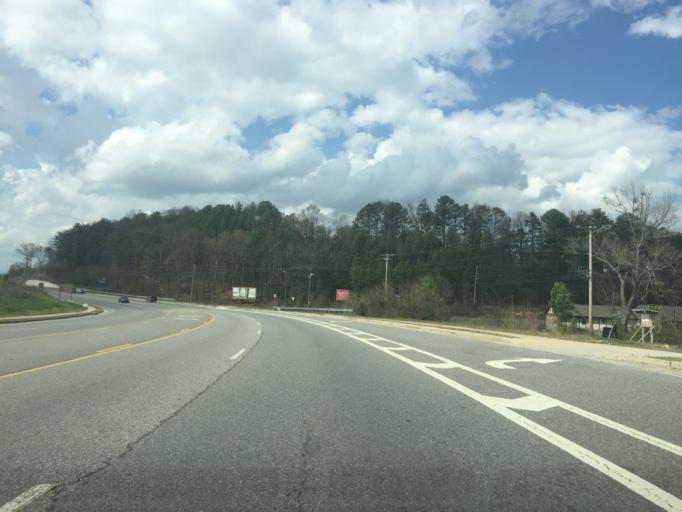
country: US
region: Georgia
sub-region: Catoosa County
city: Indian Springs
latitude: 34.9848
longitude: -85.1872
